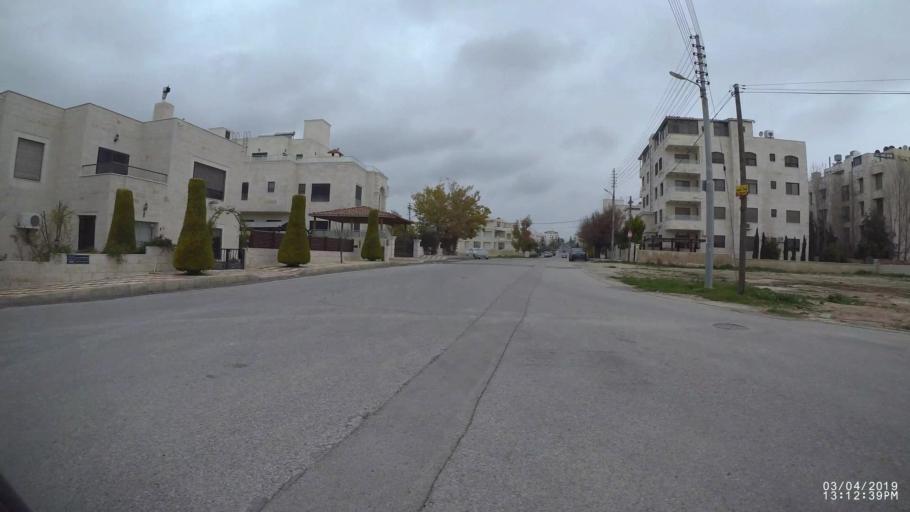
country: JO
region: Amman
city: Wadi as Sir
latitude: 31.9597
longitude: 35.8262
